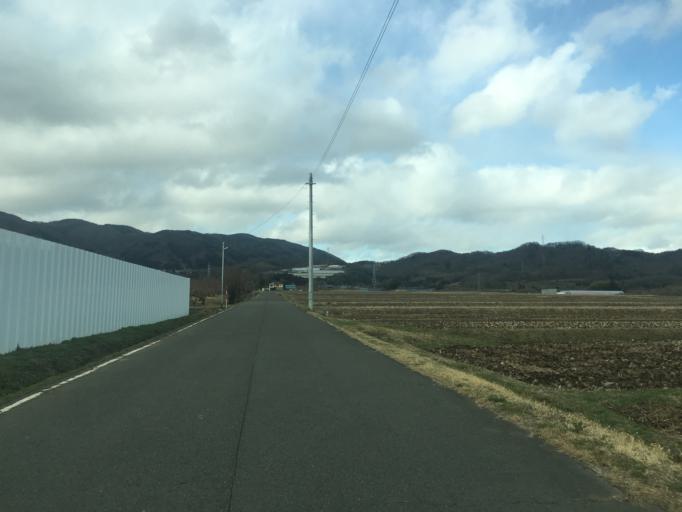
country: JP
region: Fukushima
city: Yanagawamachi-saiwaicho
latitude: 37.8817
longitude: 140.5820
